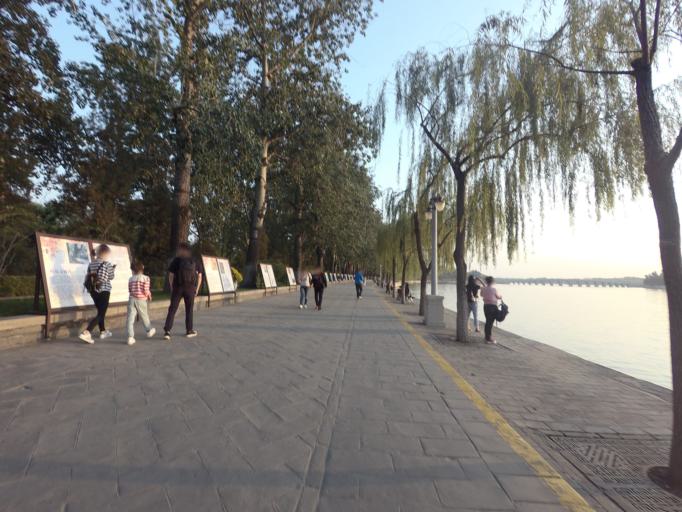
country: CN
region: Beijing
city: Haidian
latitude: 39.9929
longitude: 116.2745
